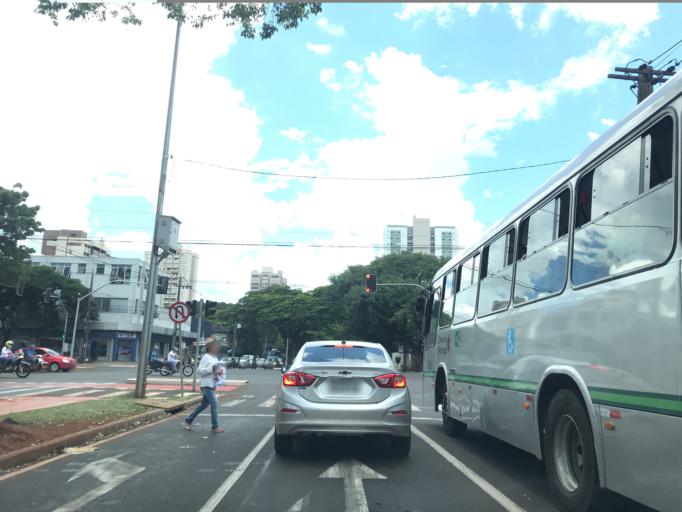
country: BR
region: Parana
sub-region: Maringa
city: Maringa
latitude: -23.4144
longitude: -51.9258
